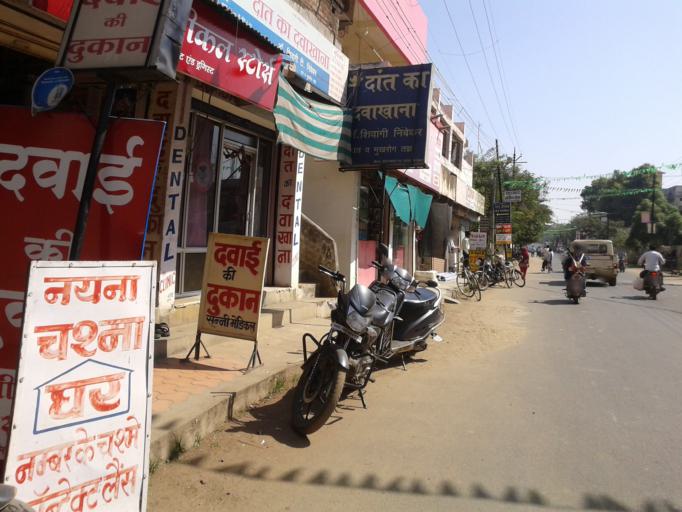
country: IN
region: Maharashtra
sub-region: Gondiya
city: Gondia
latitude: 21.4640
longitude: 80.1919
